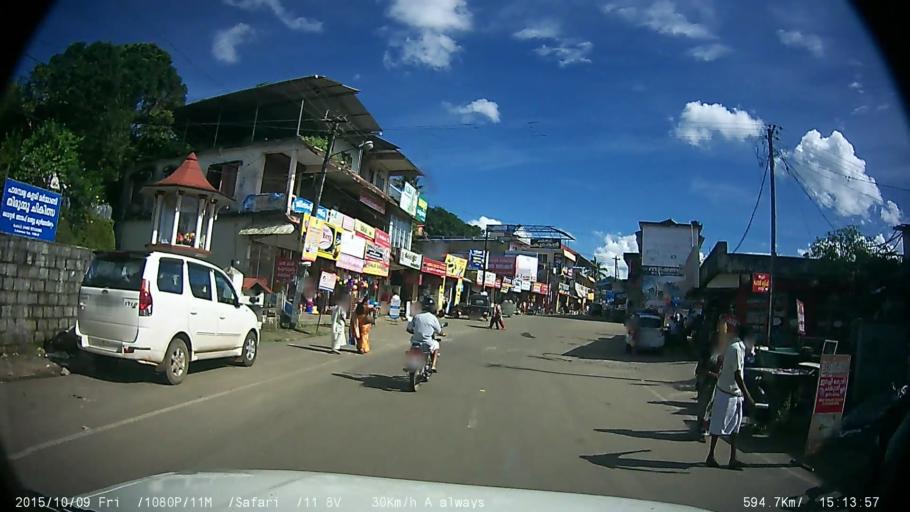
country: IN
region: Kerala
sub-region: Ernakulam
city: Piravam
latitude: 9.8642
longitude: 76.5934
